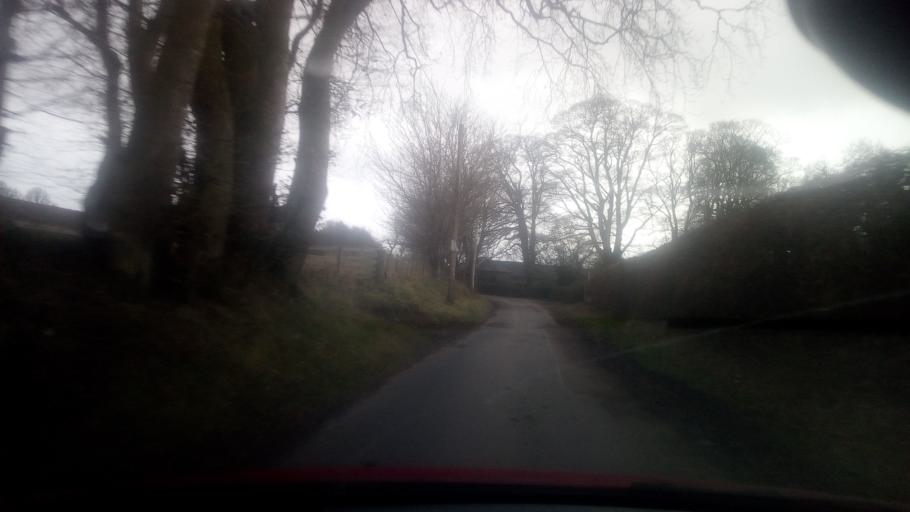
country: GB
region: Scotland
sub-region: The Scottish Borders
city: Jedburgh
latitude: 55.4723
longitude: -2.5378
